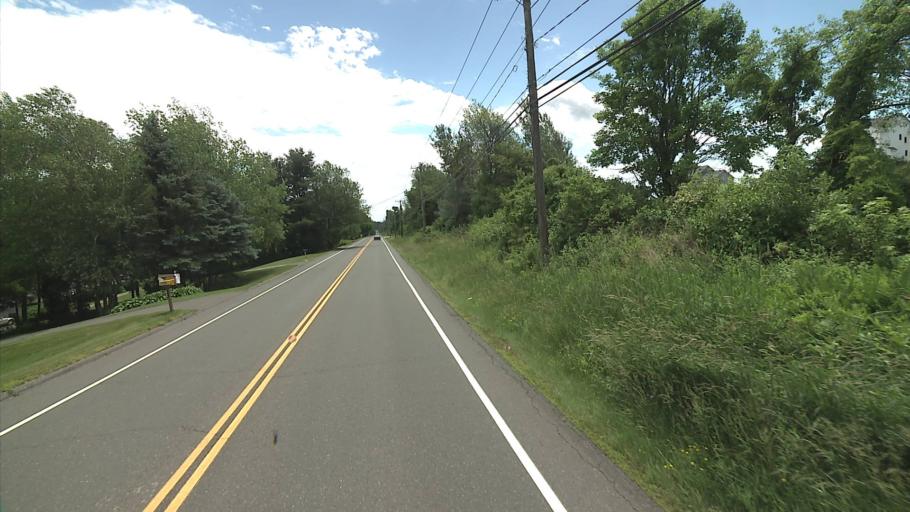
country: US
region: Connecticut
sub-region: Litchfield County
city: Watertown
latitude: 41.6401
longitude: -73.1445
